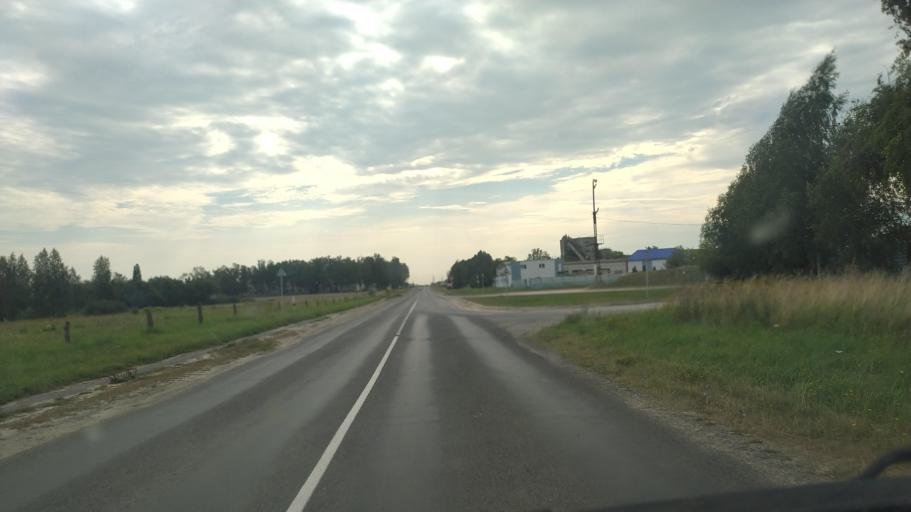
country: BY
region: Brest
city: Byaroza
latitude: 52.5530
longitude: 24.9306
